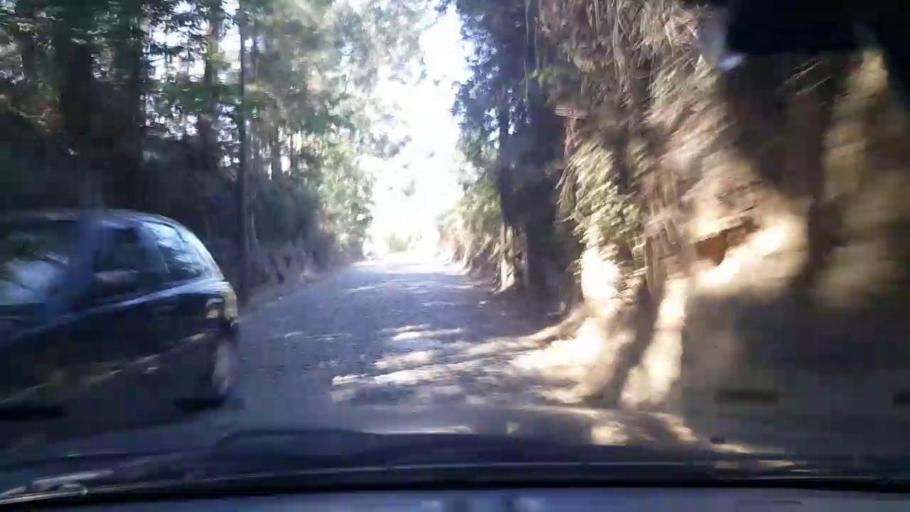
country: PT
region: Porto
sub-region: Matosinhos
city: Lavra
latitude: 41.2736
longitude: -8.6955
